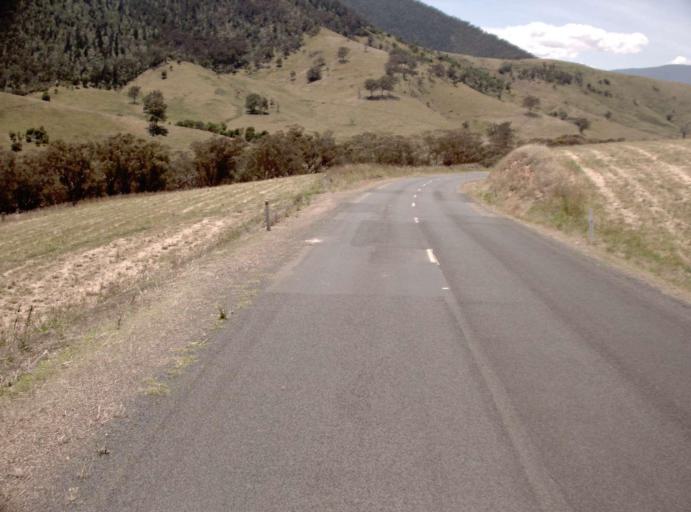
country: AU
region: Victoria
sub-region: East Gippsland
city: Bairnsdale
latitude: -37.1664
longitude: 147.6834
